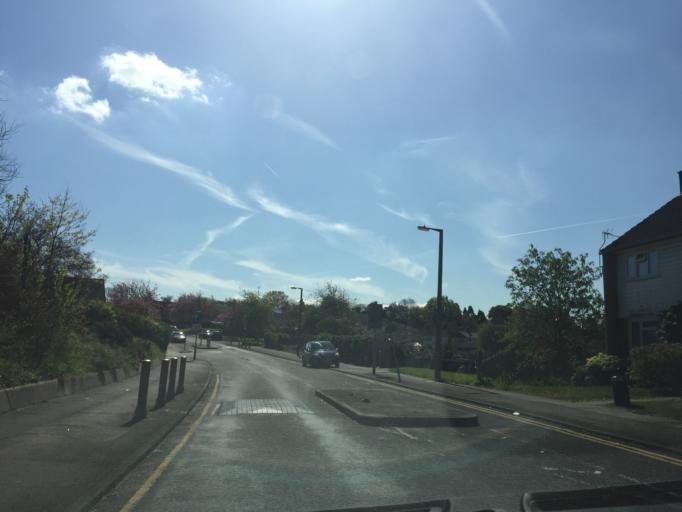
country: GB
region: England
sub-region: Essex
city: Harlow
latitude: 51.7664
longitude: 0.0811
